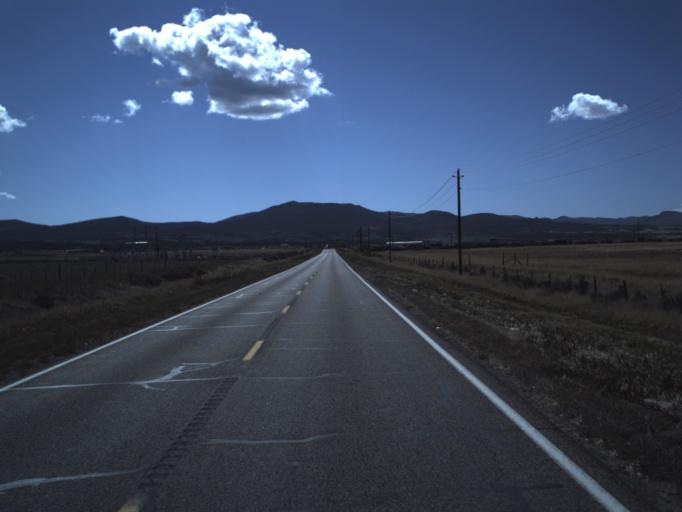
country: US
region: Utah
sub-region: Washington County
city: Enterprise
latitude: 37.6156
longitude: -113.6612
